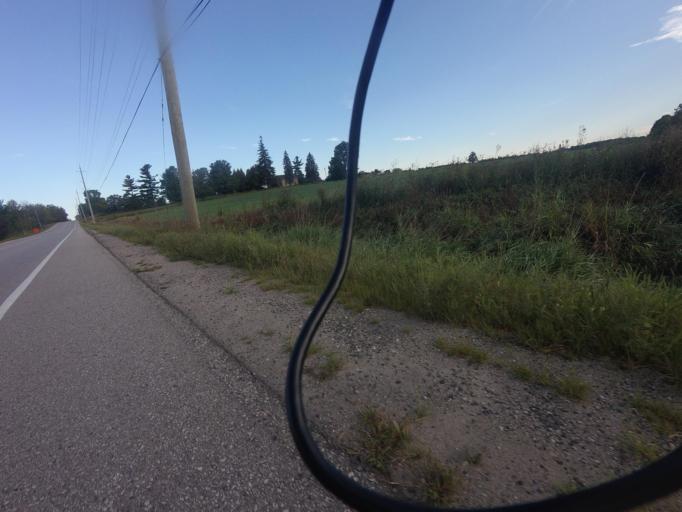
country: CA
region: Ontario
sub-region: Wellington County
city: Guelph
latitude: 43.5726
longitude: -80.3255
